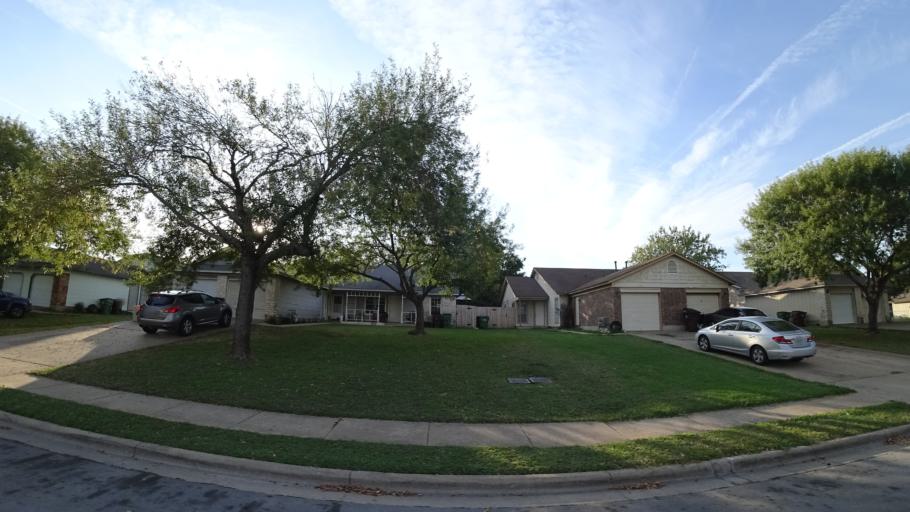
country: US
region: Texas
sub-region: Williamson County
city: Round Rock
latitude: 30.5038
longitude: -97.6614
